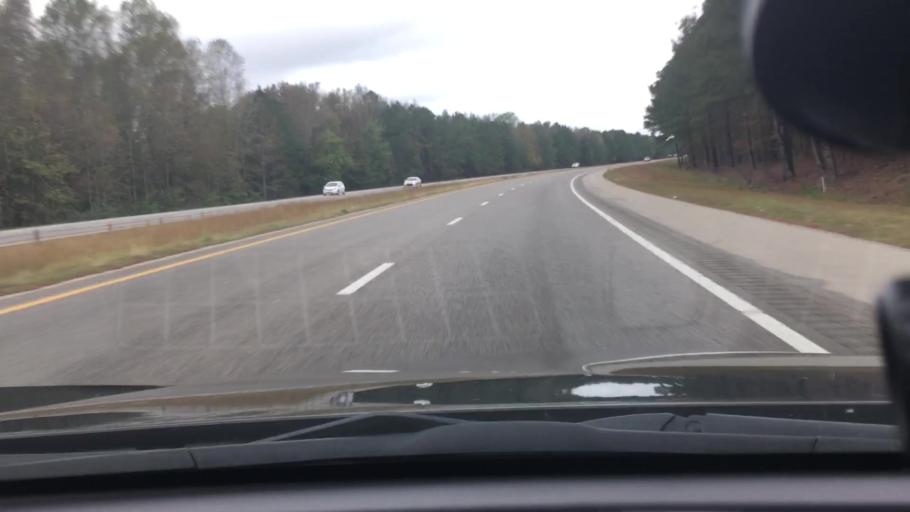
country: US
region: North Carolina
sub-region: Wilson County
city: Wilson
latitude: 35.6716
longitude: -77.8302
